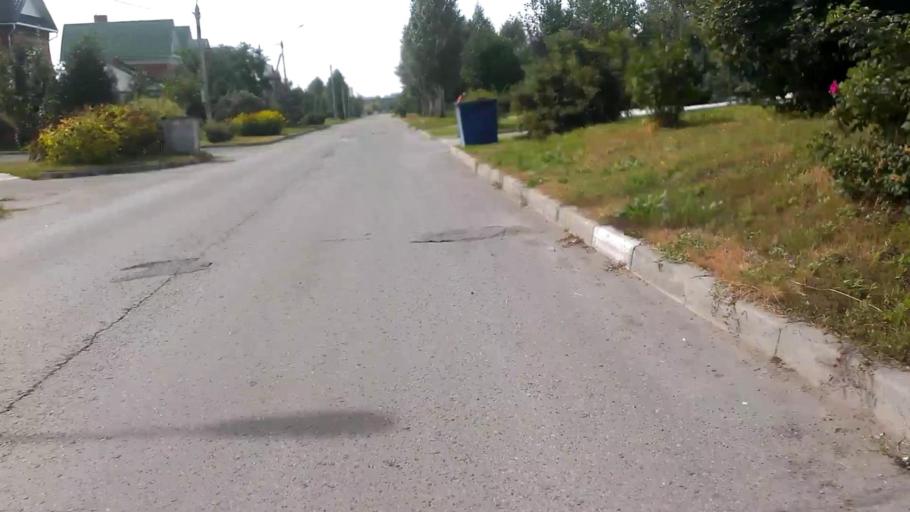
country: RU
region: Altai Krai
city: Novosilikatnyy
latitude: 53.3560
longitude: 83.6539
